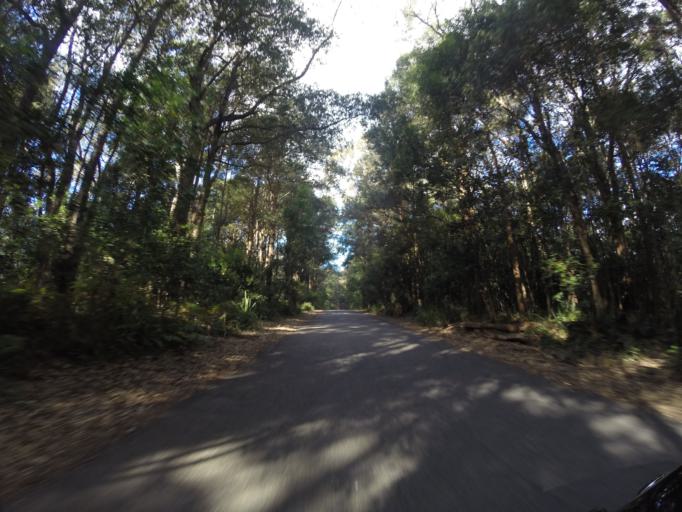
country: AU
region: New South Wales
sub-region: Wollongong
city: Mount Keira
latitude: -34.3971
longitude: 150.8508
